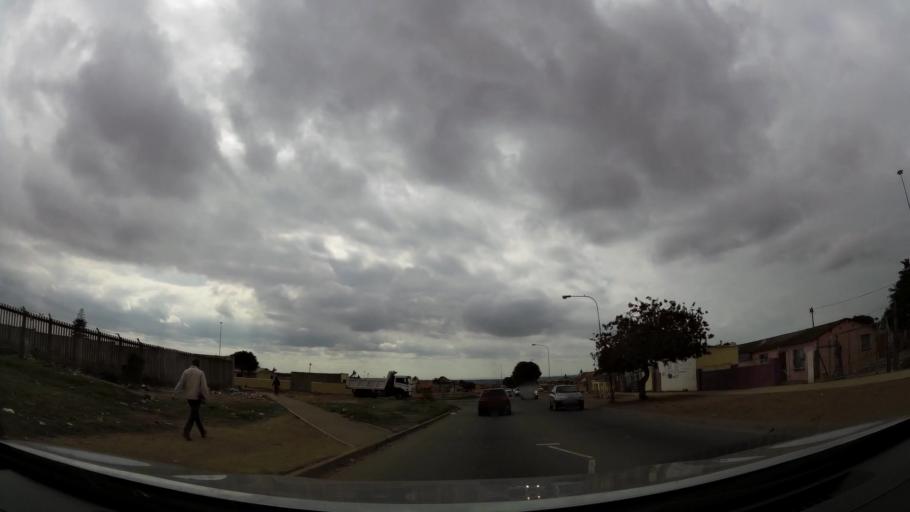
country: ZA
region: Eastern Cape
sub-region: Nelson Mandela Bay Metropolitan Municipality
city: Port Elizabeth
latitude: -33.8742
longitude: 25.5629
